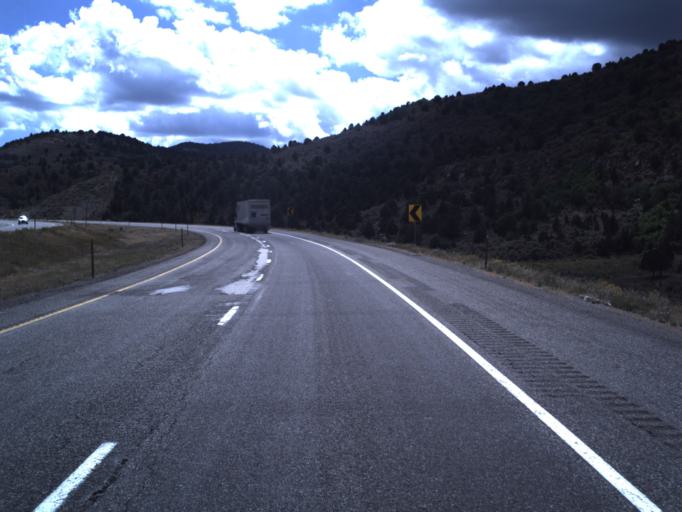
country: US
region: Utah
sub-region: Sevier County
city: Salina
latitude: 38.8141
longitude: -111.5367
